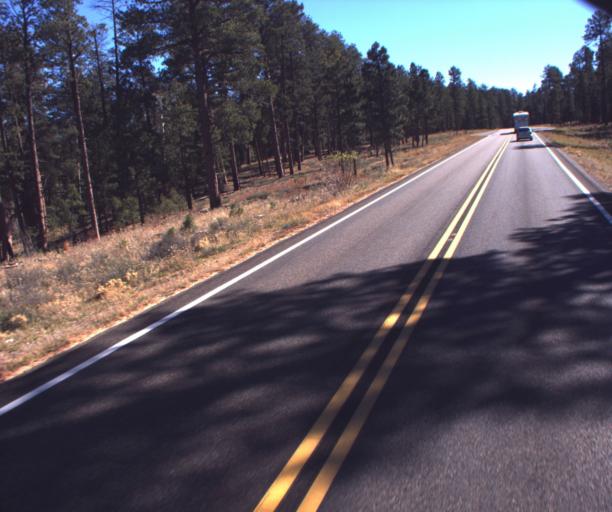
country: US
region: Arizona
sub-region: Coconino County
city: Fredonia
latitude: 36.6666
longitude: -112.1954
